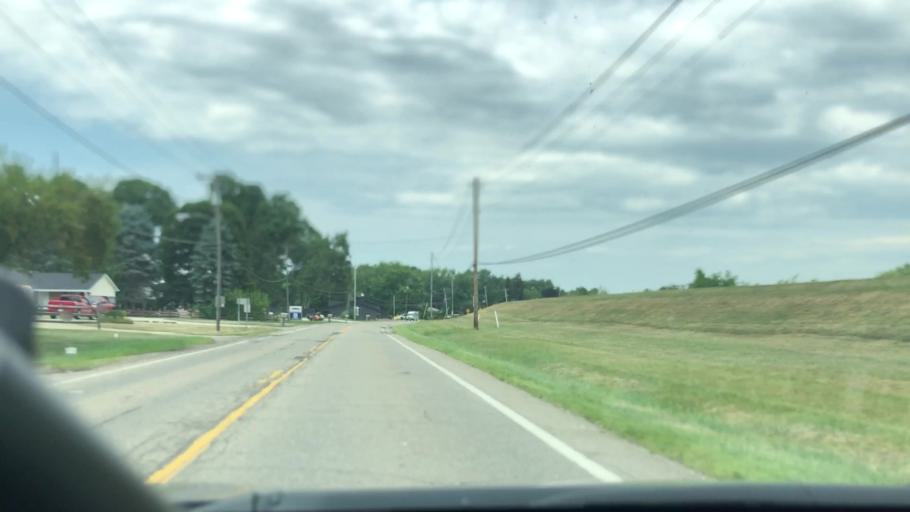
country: US
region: Ohio
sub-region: Summit County
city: New Franklin
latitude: 40.9518
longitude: -81.5338
